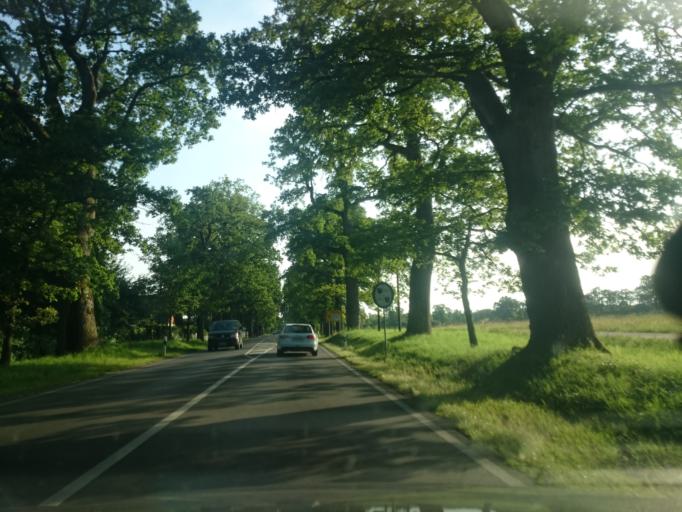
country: DE
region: Bavaria
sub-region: Upper Bavaria
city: Seefeld
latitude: 48.0444
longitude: 11.2148
